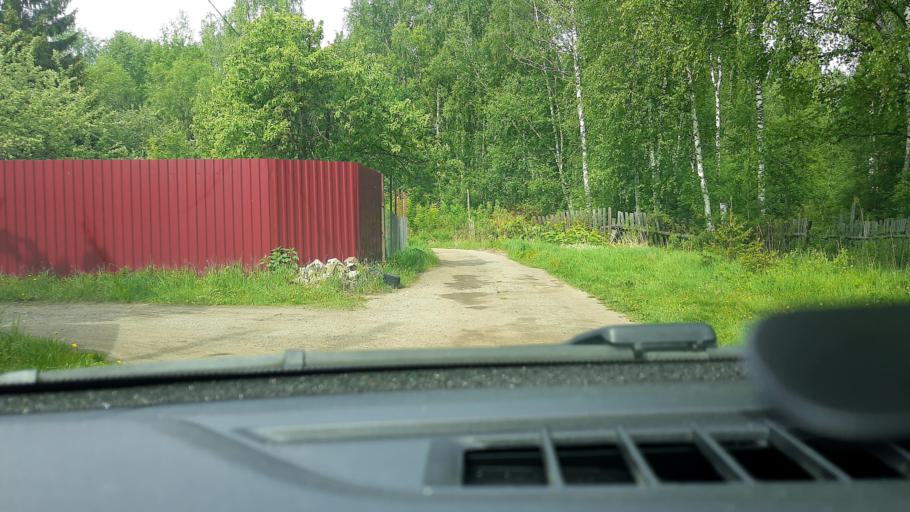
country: RU
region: Nizjnij Novgorod
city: Gorbatovka
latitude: 56.3055
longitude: 43.7672
